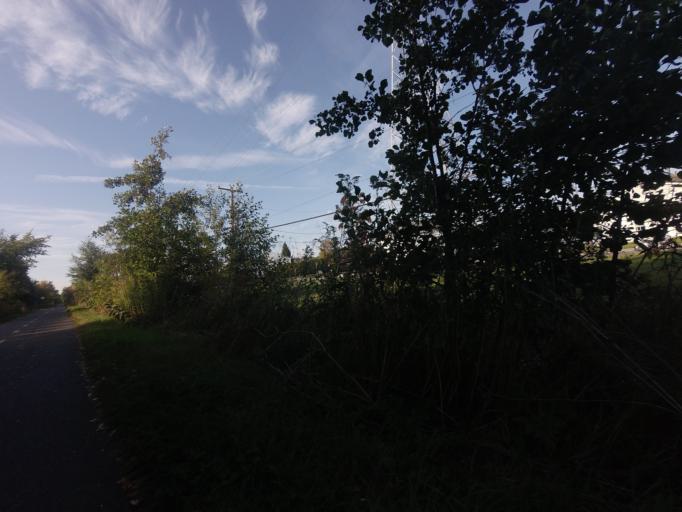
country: CA
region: Quebec
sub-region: Laurentides
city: Saint-Jerome
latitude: 45.8000
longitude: -74.0050
